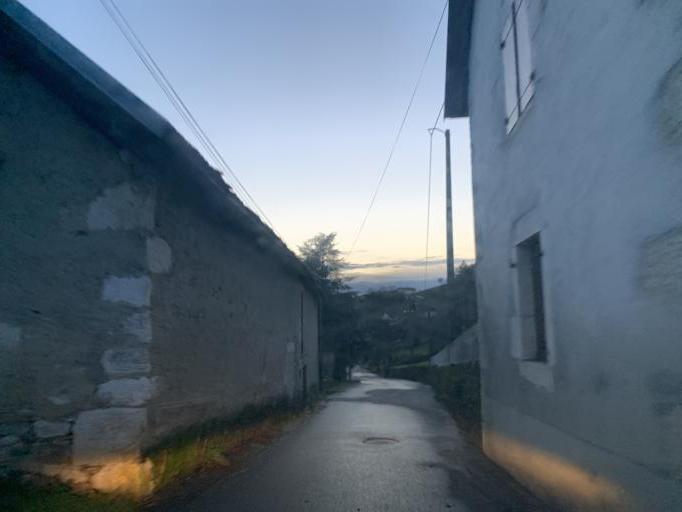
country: FR
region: Rhone-Alpes
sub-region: Departement de l'Ain
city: Belley
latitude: 45.7687
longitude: 5.7026
